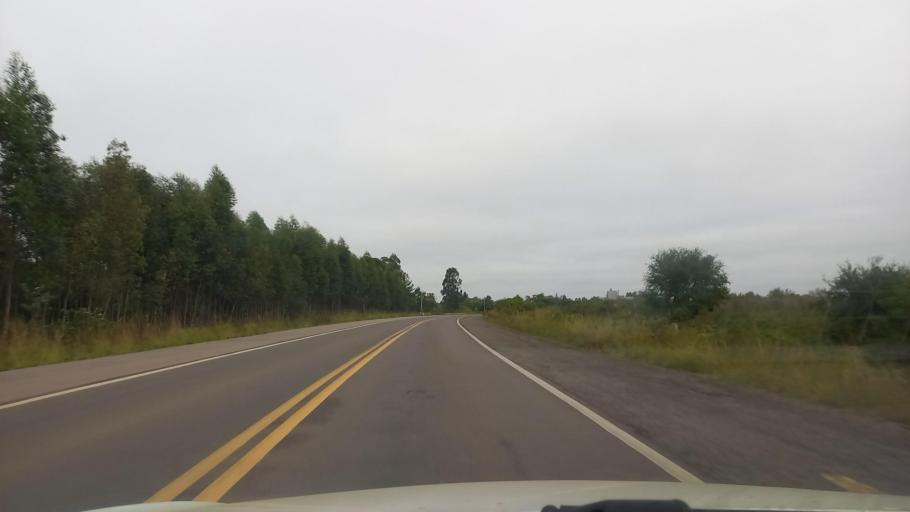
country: BR
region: Rio Grande do Sul
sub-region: Sao Pedro Do Sul
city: Sao Pedro do Sul
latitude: -29.7988
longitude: -54.1207
